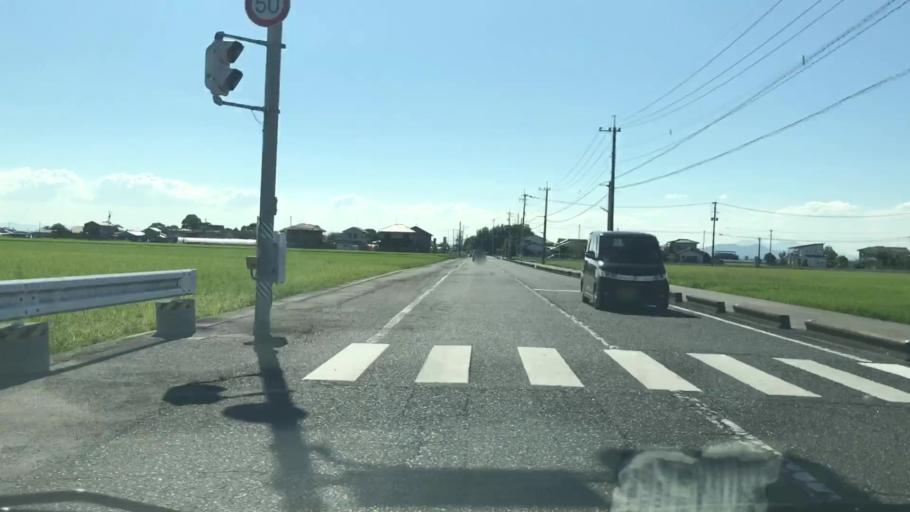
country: JP
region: Saga Prefecture
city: Okawa
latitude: 33.2201
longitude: 130.3443
